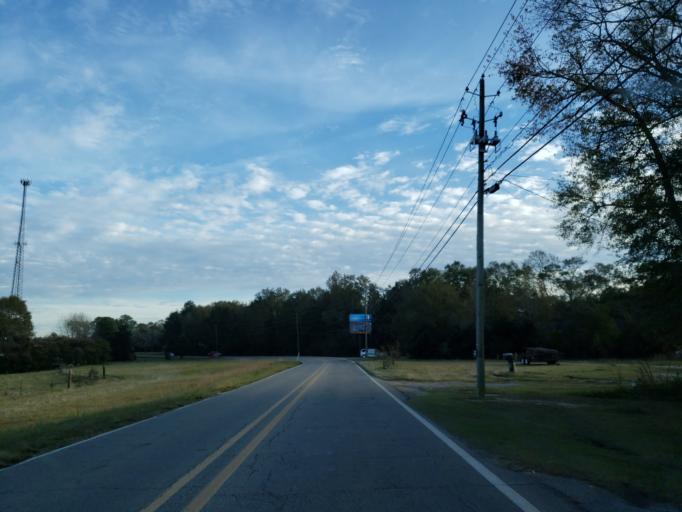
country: US
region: Mississippi
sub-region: Lamar County
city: Purvis
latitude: 31.1575
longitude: -89.4199
